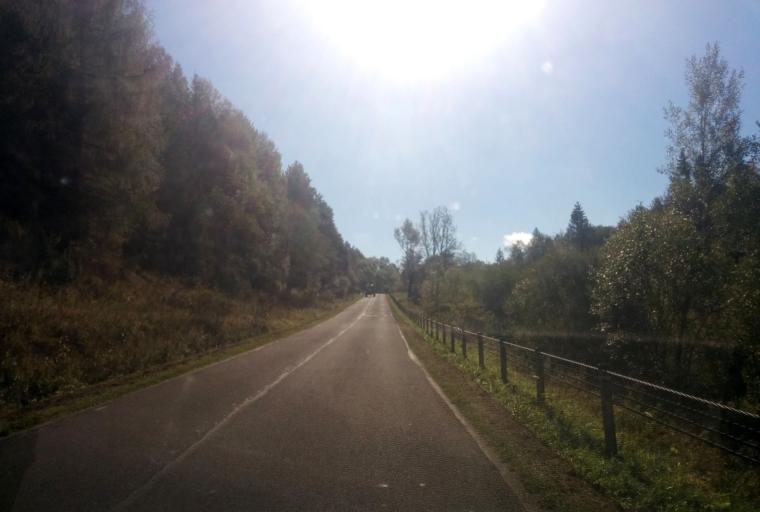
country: PL
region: Subcarpathian Voivodeship
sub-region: Powiat bieszczadzki
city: Lutowiska
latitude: 49.1394
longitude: 22.5702
